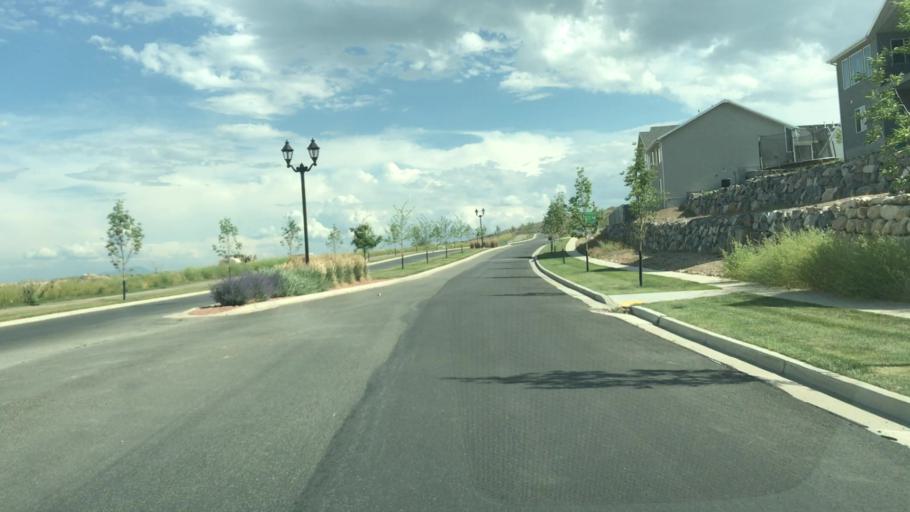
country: US
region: Utah
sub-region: Utah County
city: Saratoga Springs
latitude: 40.3052
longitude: -111.8995
